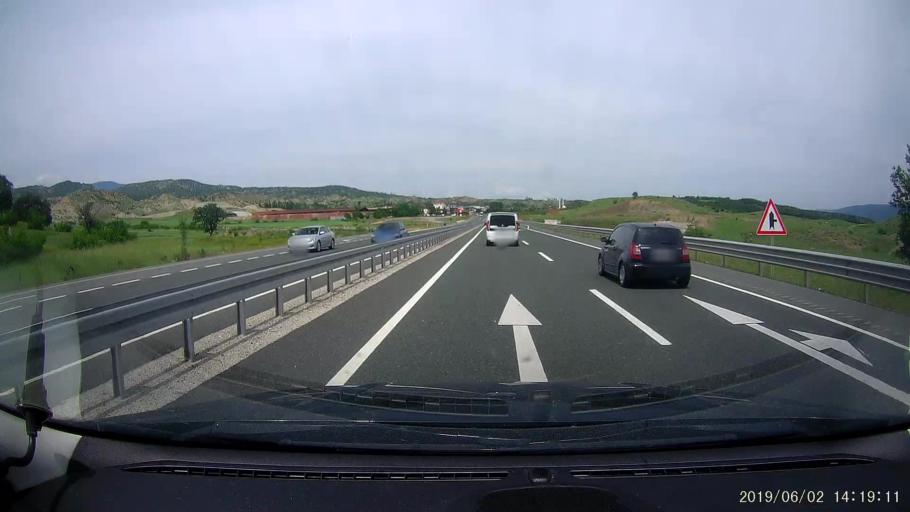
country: TR
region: Kastamonu
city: Tosya
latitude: 40.9620
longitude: 33.9718
